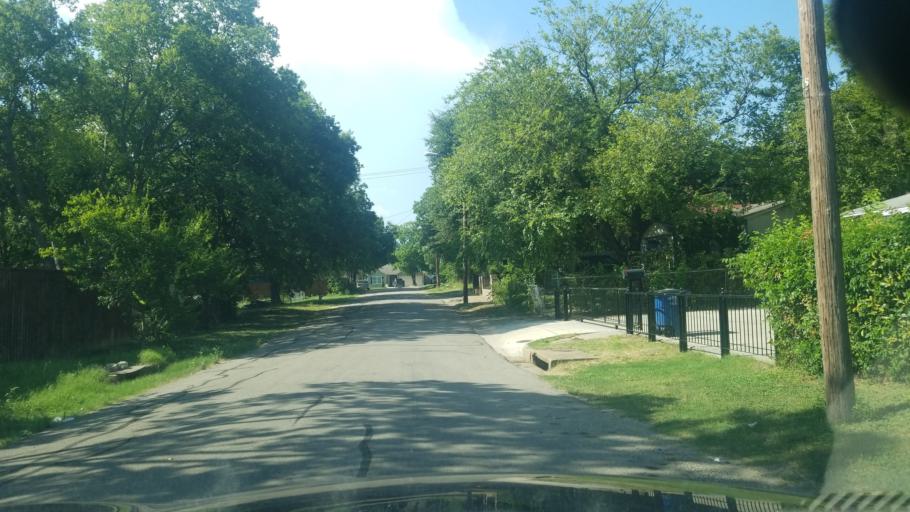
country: US
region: Texas
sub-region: Dallas County
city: Dallas
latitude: 32.7214
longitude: -96.8074
